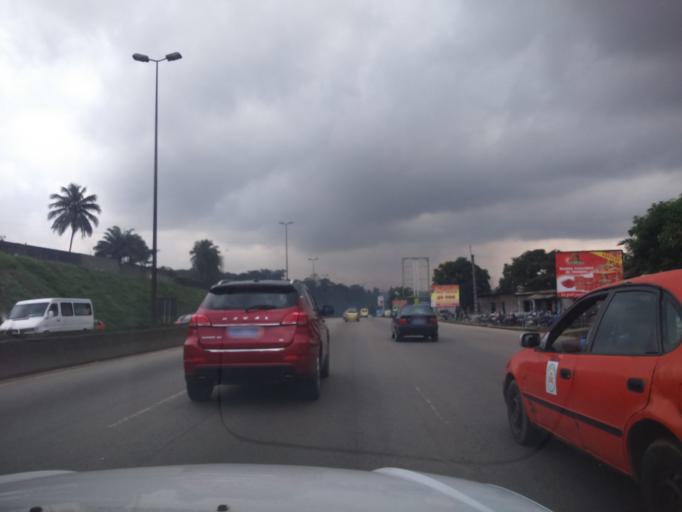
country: CI
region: Lagunes
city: Abidjan
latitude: 5.3592
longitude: -4.0623
